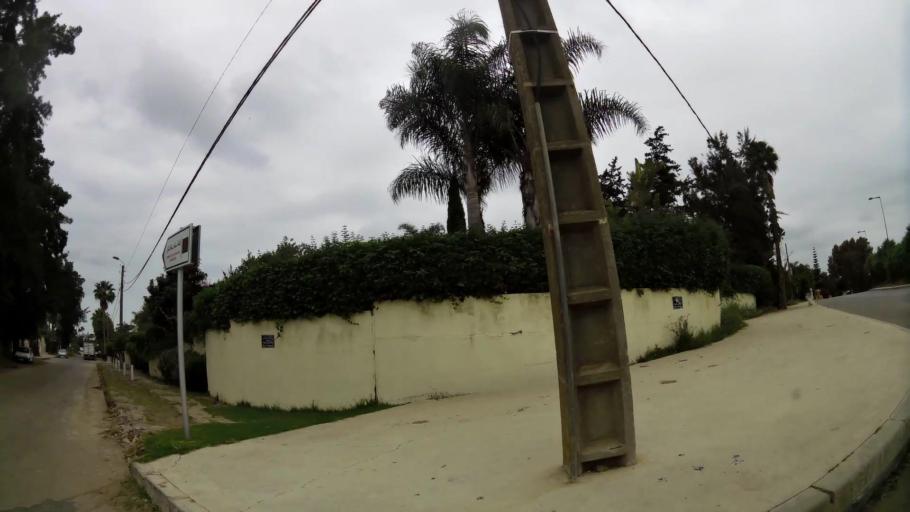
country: MA
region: Rabat-Sale-Zemmour-Zaer
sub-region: Rabat
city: Rabat
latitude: 33.9616
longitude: -6.8124
